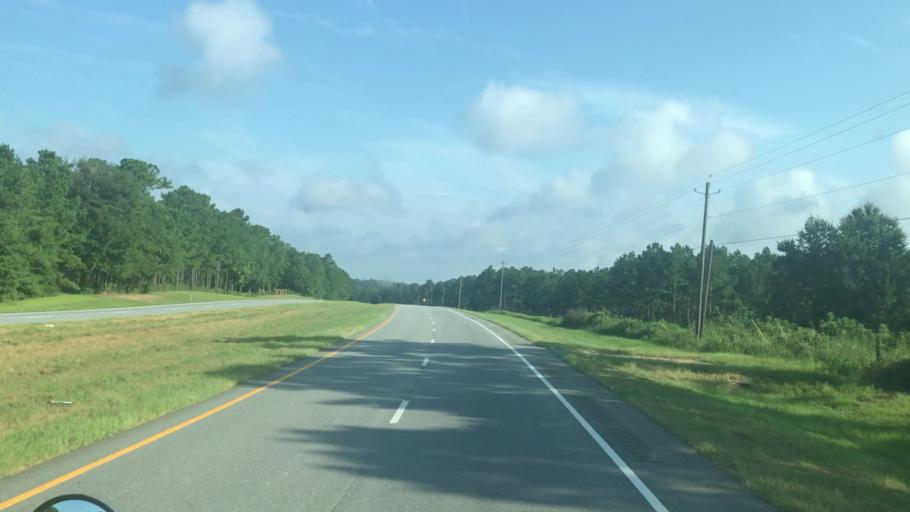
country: US
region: Georgia
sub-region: Decatur County
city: Bainbridge
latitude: 30.8350
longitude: -84.5300
